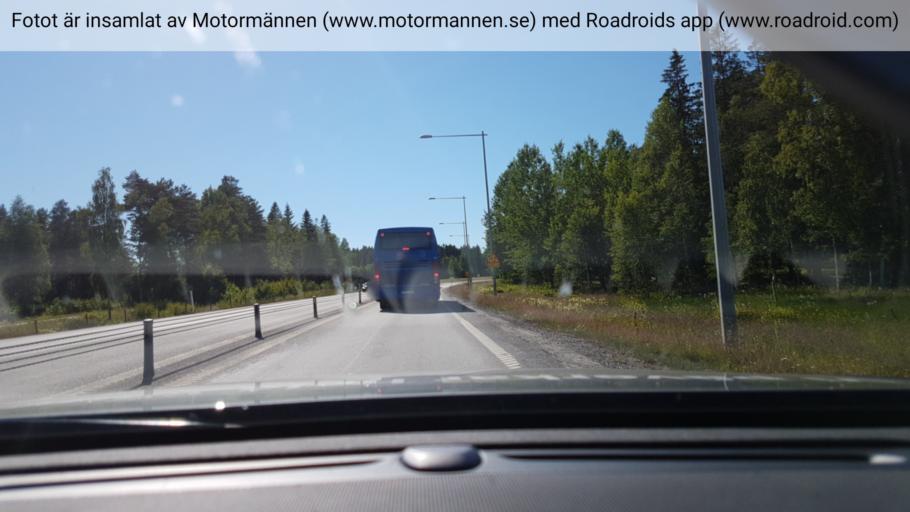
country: SE
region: Vaesterbotten
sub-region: Umea Kommun
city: Ersmark
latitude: 63.8480
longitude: 20.3475
